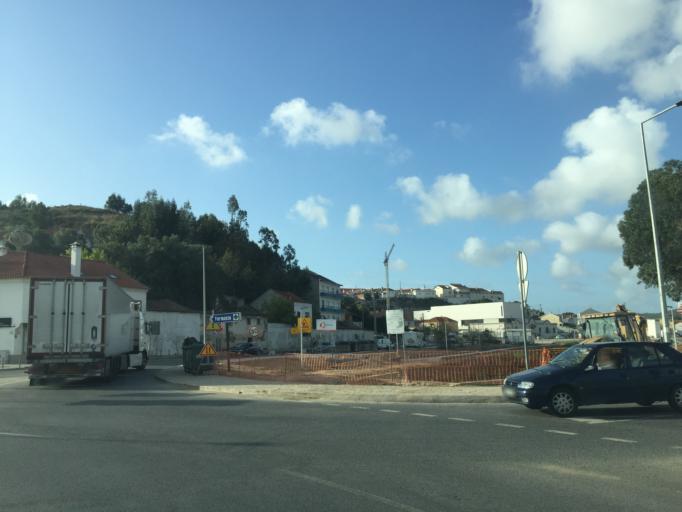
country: PT
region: Lisbon
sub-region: Torres Vedras
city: Torres Vedras
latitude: 39.0983
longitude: -9.2601
